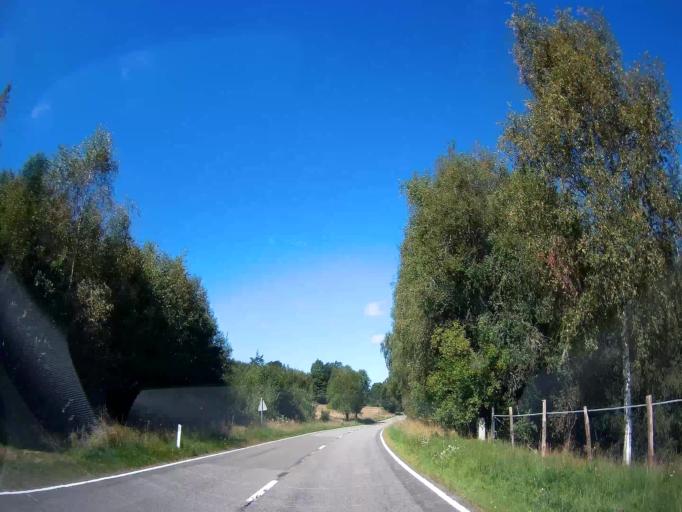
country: BE
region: Wallonia
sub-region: Province du Luxembourg
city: Bertogne
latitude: 50.1150
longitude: 5.6268
